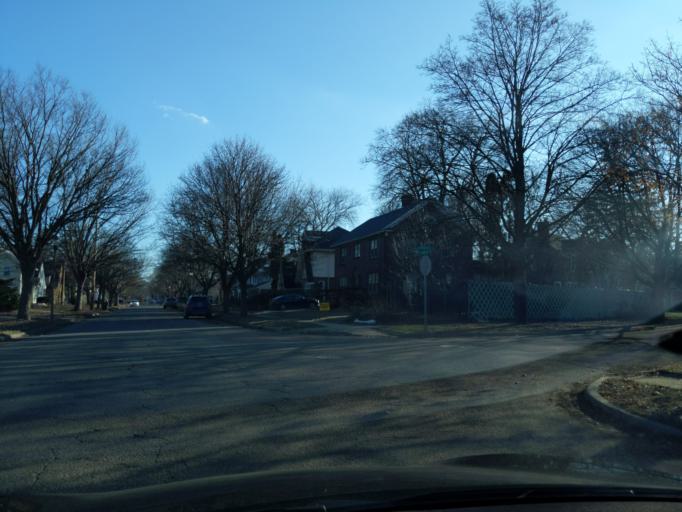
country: US
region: Michigan
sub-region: Ingham County
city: Lansing
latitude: 42.7289
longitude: -84.5727
